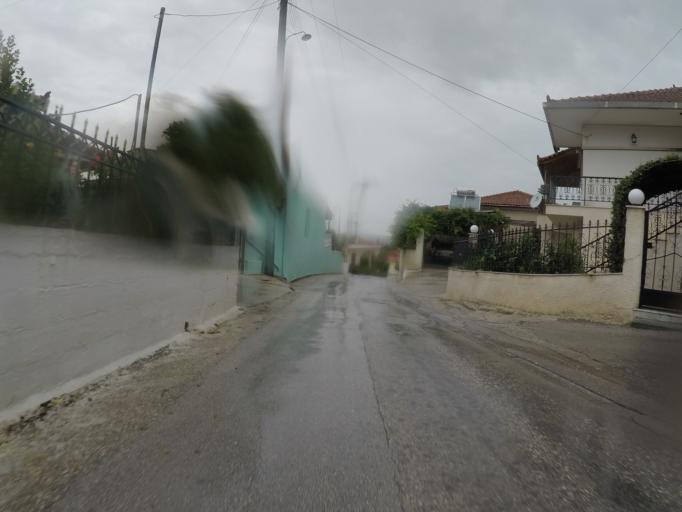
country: GR
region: Peloponnese
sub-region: Nomos Korinthias
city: Arkhaia Korinthos
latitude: 37.9071
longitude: 22.8834
